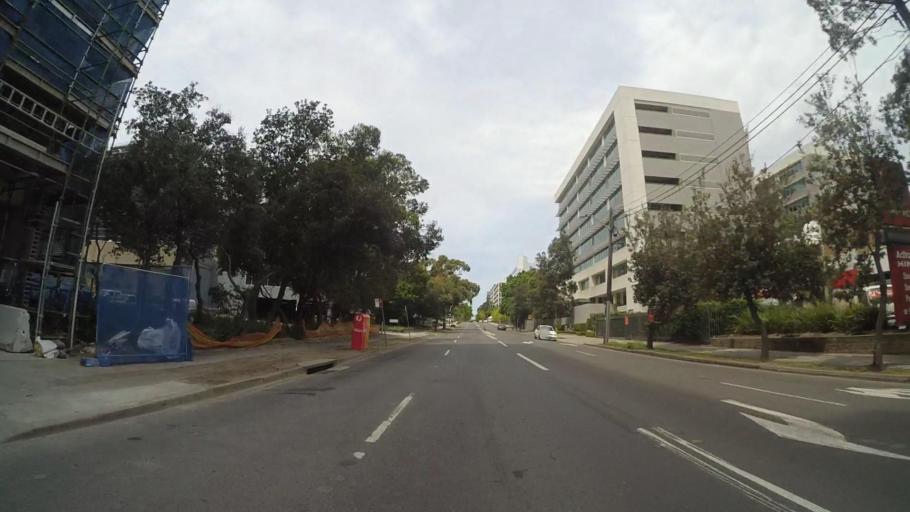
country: AU
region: New South Wales
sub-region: Botany Bay
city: Mascot
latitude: -33.9239
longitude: 151.1844
